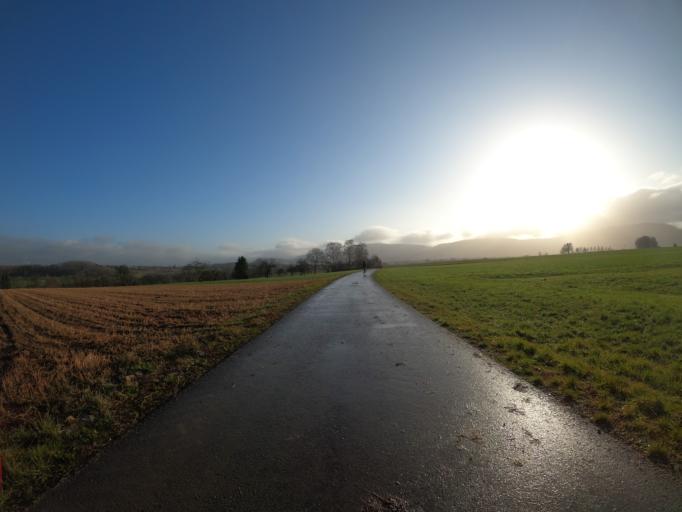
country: DE
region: Baden-Wuerttemberg
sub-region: Regierungsbezirk Stuttgart
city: Boll
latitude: 48.6572
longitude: 9.6192
